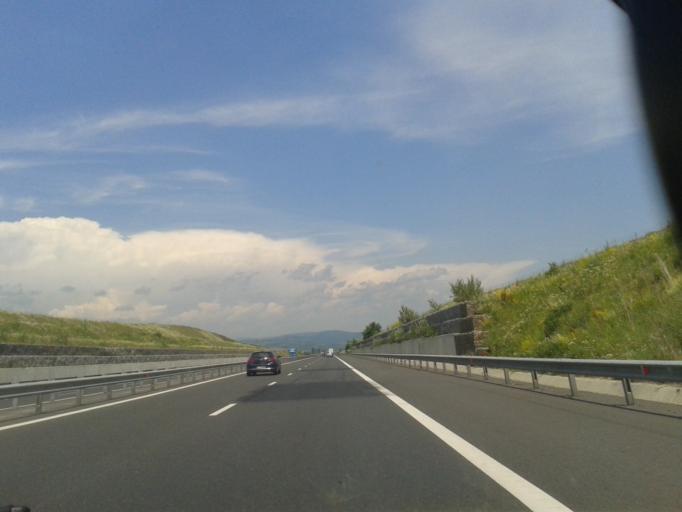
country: RO
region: Hunedoara
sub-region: Comuna Turdas
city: Turdas
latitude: 45.8497
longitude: 23.1346
